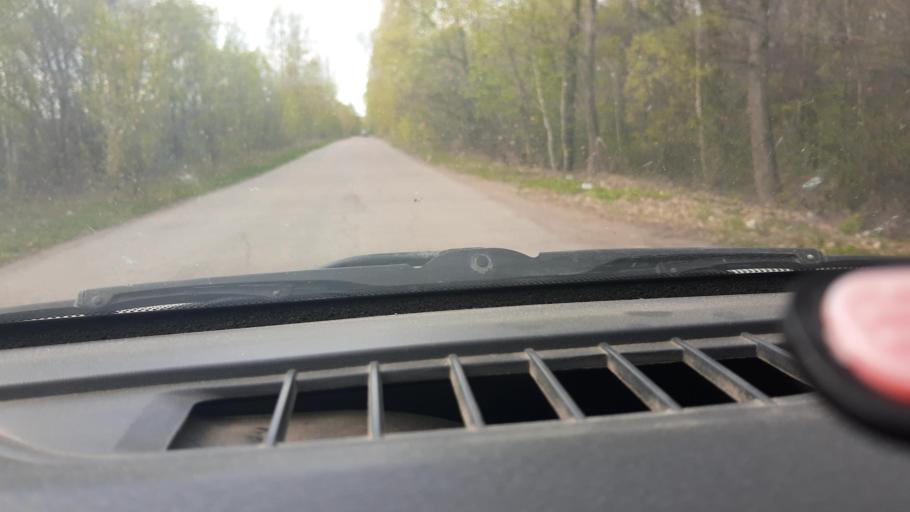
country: RU
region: Bashkortostan
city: Avdon
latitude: 54.6569
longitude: 55.8238
